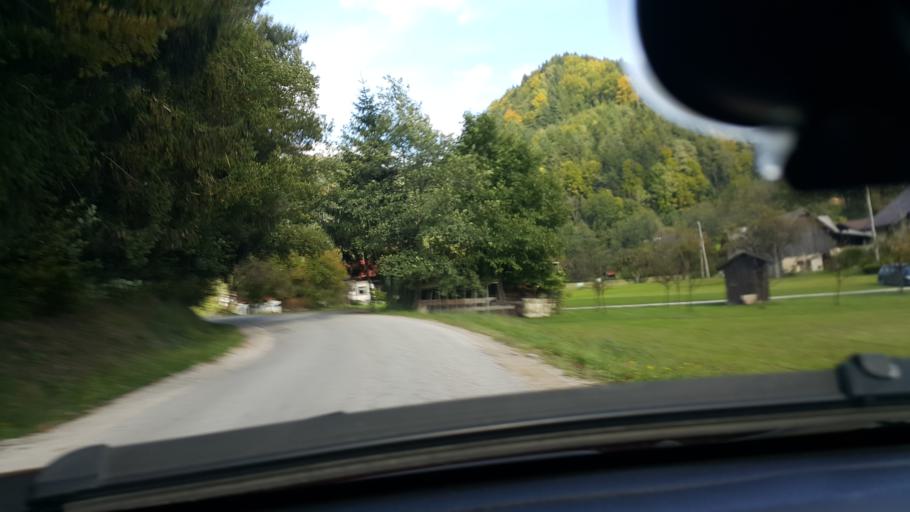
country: SI
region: Vitanje
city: Vitanje
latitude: 46.3896
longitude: 15.3060
